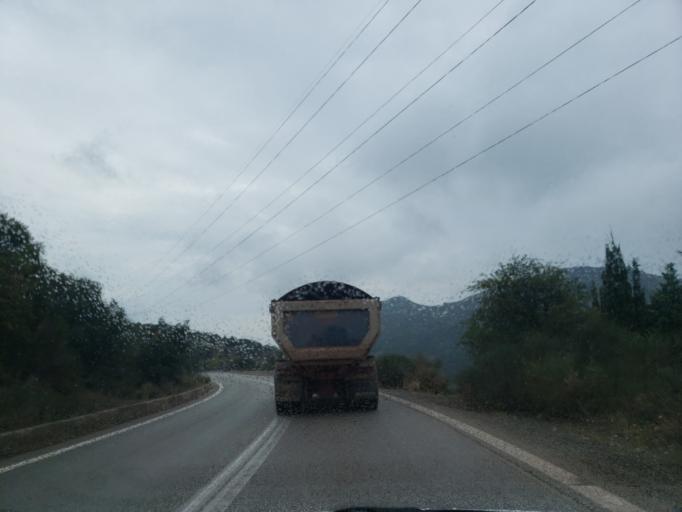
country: GR
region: Central Greece
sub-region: Nomos Fokidos
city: Amfissa
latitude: 38.5776
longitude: 22.3936
